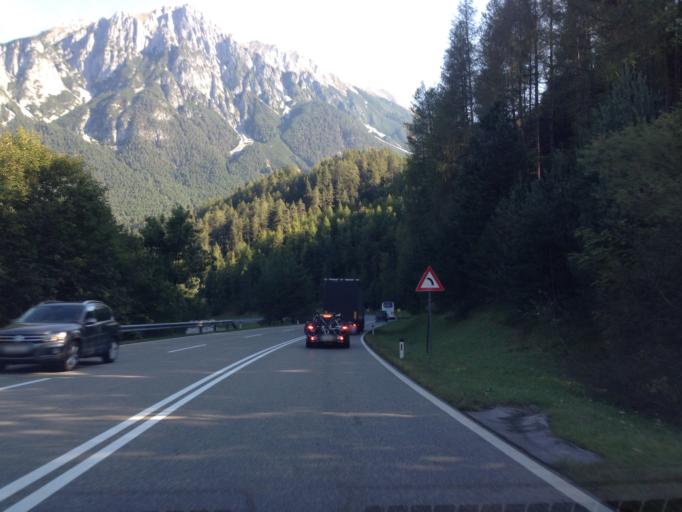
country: AT
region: Tyrol
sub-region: Politischer Bezirk Imst
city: Nassereith
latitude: 47.3040
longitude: 10.8565
